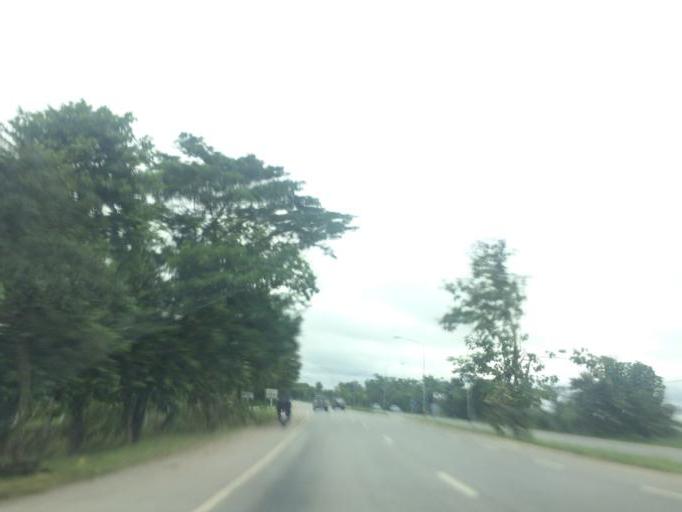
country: TH
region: Chiang Rai
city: Mae Lao
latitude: 19.7858
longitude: 99.7453
